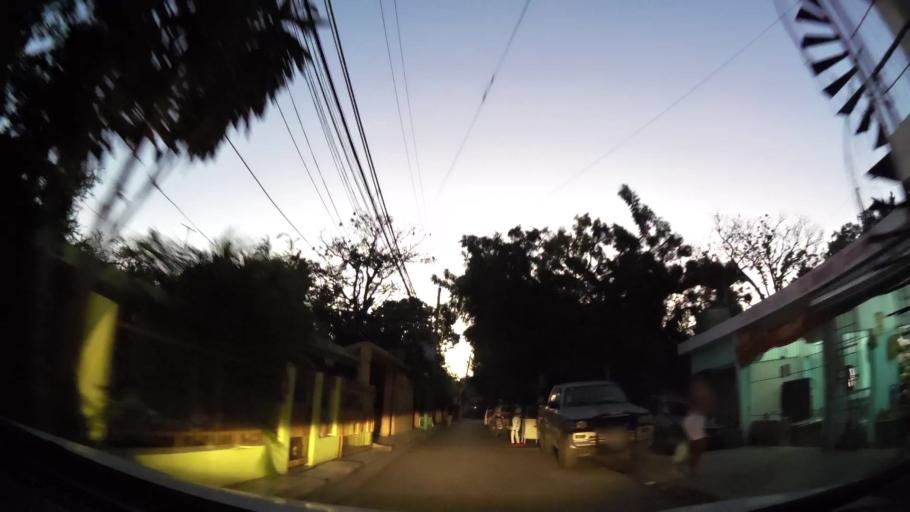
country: DO
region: Santo Domingo
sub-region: Santo Domingo
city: Santo Domingo Este
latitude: 18.5034
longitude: -69.8399
